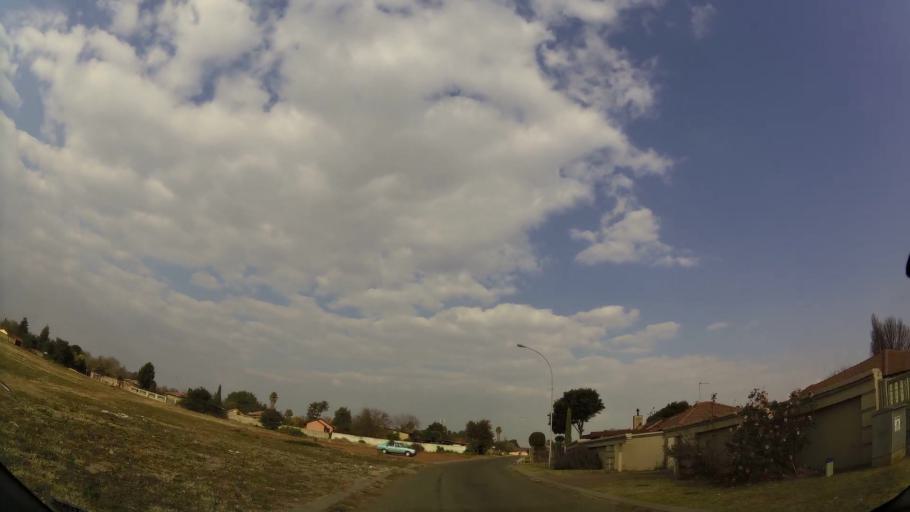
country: ZA
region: Gauteng
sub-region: Ekurhuleni Metropolitan Municipality
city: Benoni
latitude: -26.1207
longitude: 28.3698
